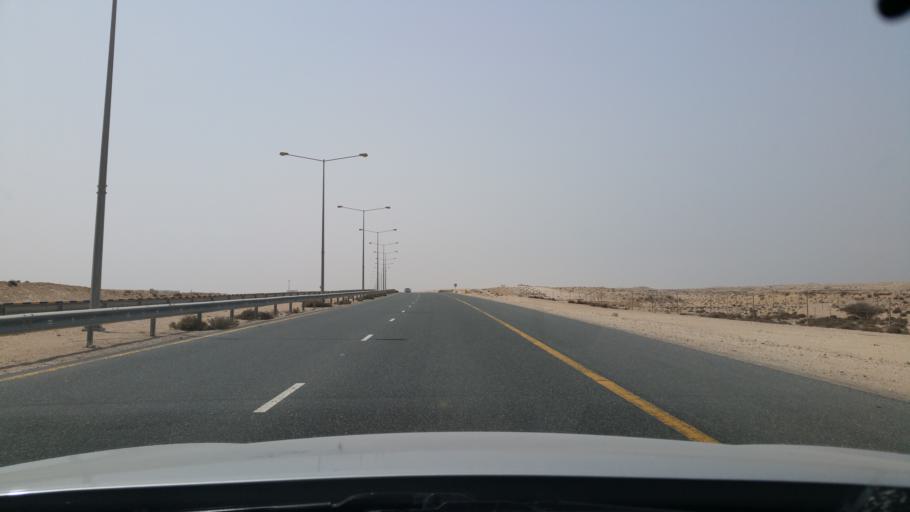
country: QA
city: Umm Bab
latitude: 25.2852
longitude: 50.7906
